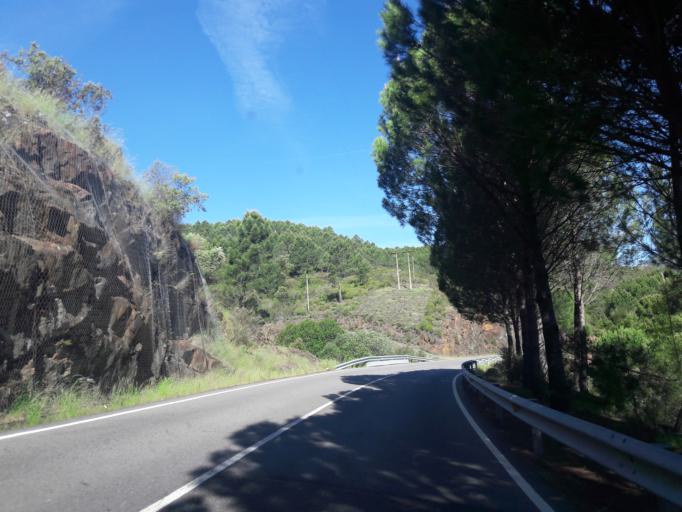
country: ES
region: Castille and Leon
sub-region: Provincia de Salamanca
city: Herguijuela de la Sierra
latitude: 40.4069
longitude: -6.0920
